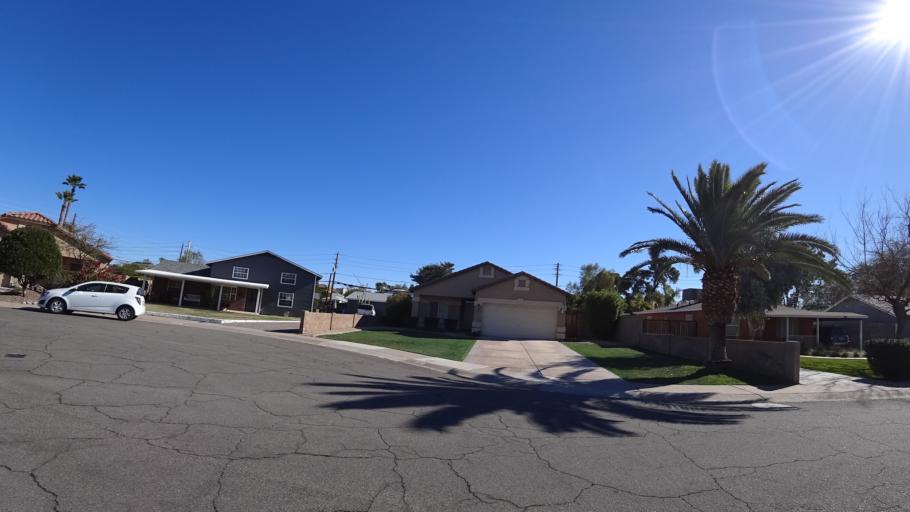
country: US
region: Arizona
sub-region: Maricopa County
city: Phoenix
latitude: 33.5010
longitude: -112.0400
